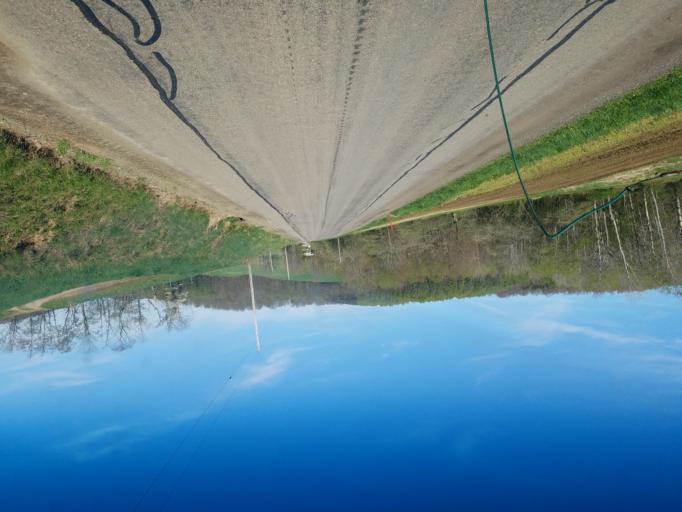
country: US
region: New York
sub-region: Allegany County
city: Andover
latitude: 41.9852
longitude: -77.7788
